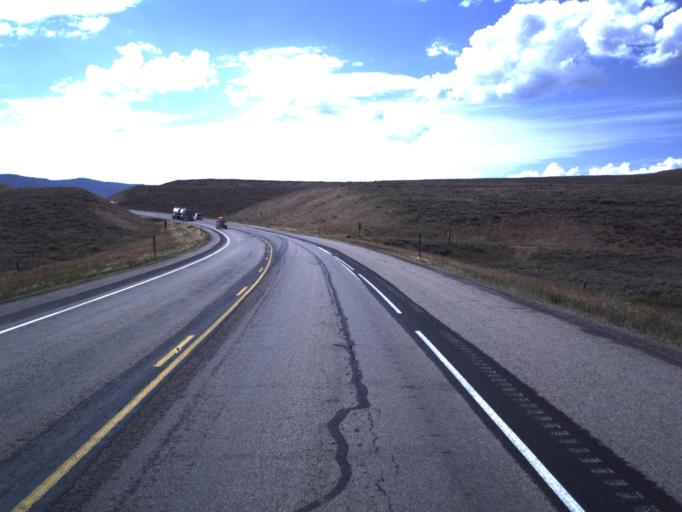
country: US
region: Utah
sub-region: Wasatch County
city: Heber
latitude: 40.2301
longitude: -111.1209
